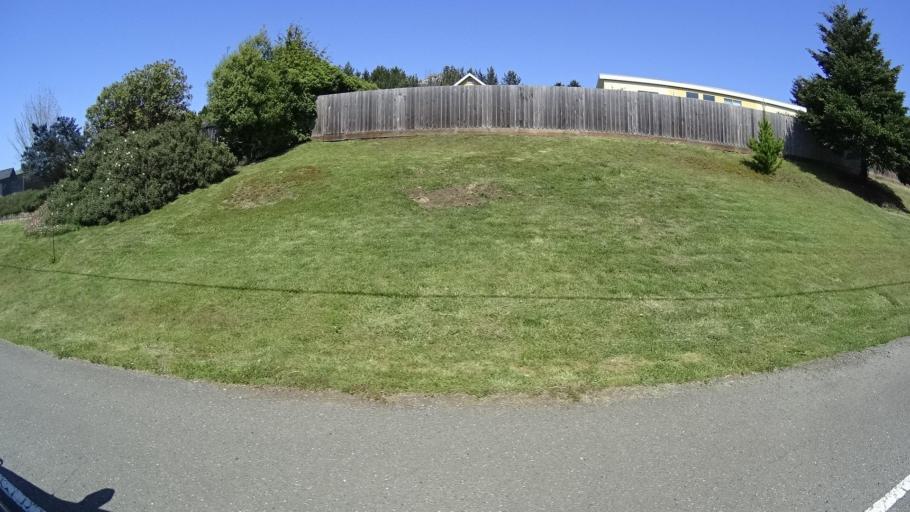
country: US
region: California
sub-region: Humboldt County
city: Hydesville
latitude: 40.5598
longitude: -124.1243
